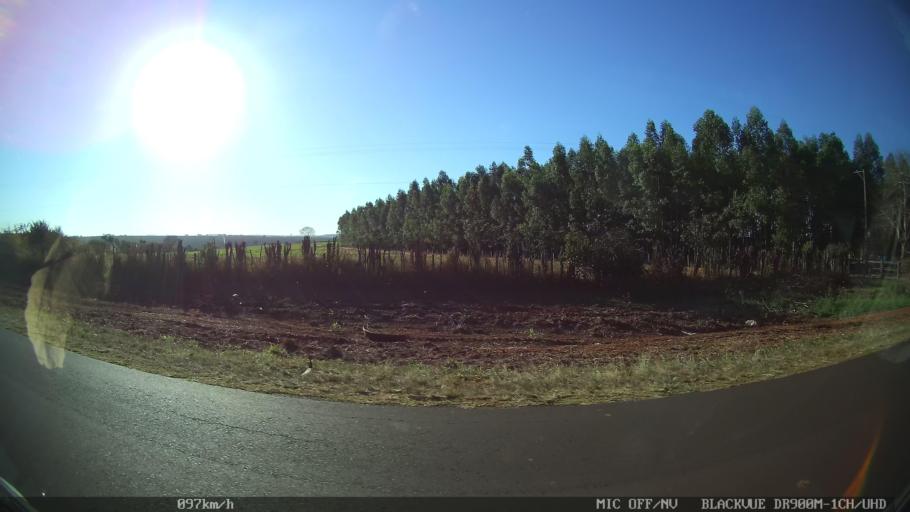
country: BR
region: Sao Paulo
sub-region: Guapiacu
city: Guapiacu
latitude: -20.7497
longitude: -49.1329
